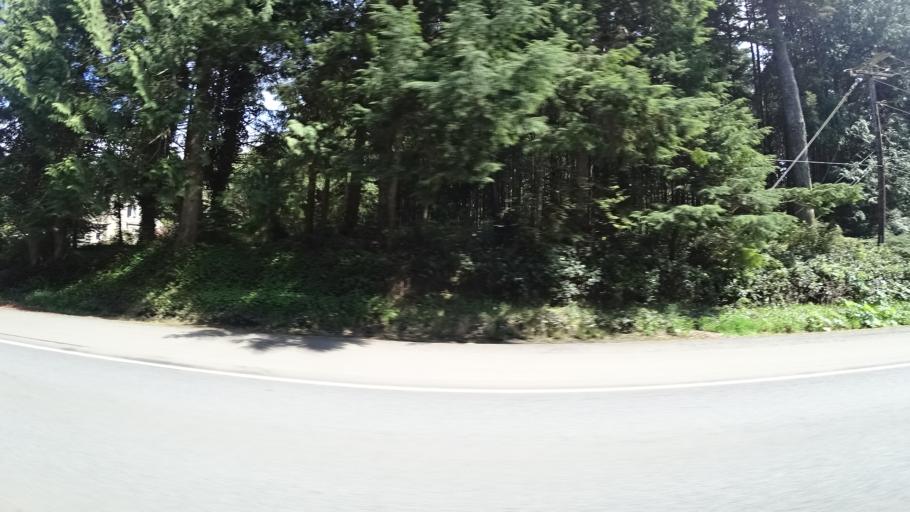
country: US
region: Oregon
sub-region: Lincoln County
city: Lincoln Beach
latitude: 44.8309
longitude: -124.0569
